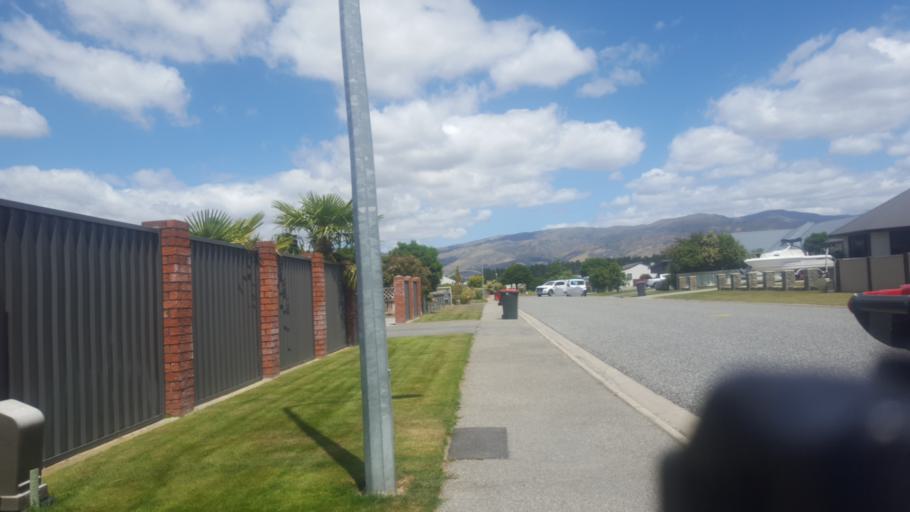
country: NZ
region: Otago
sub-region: Queenstown-Lakes District
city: Wanaka
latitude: -45.0499
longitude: 169.1988
